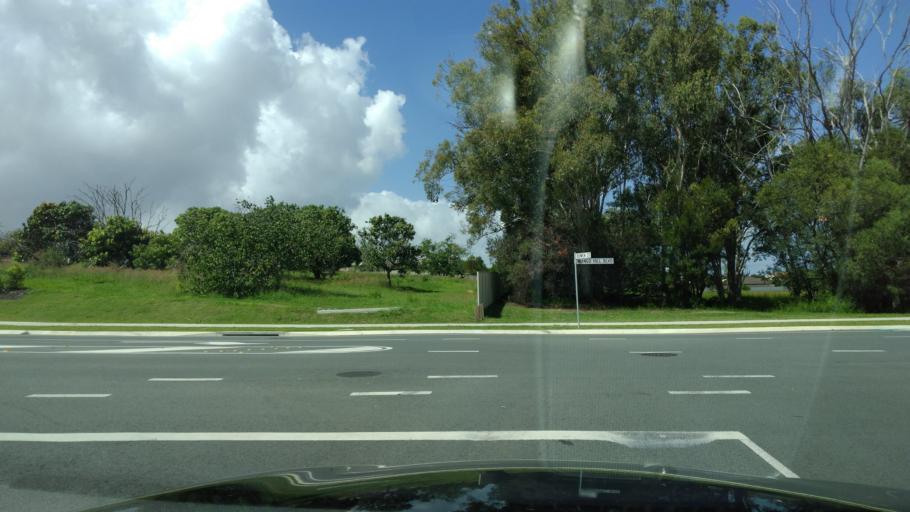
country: AU
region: Queensland
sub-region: Moreton Bay
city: Mango Hill
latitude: -27.2429
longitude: 153.0285
